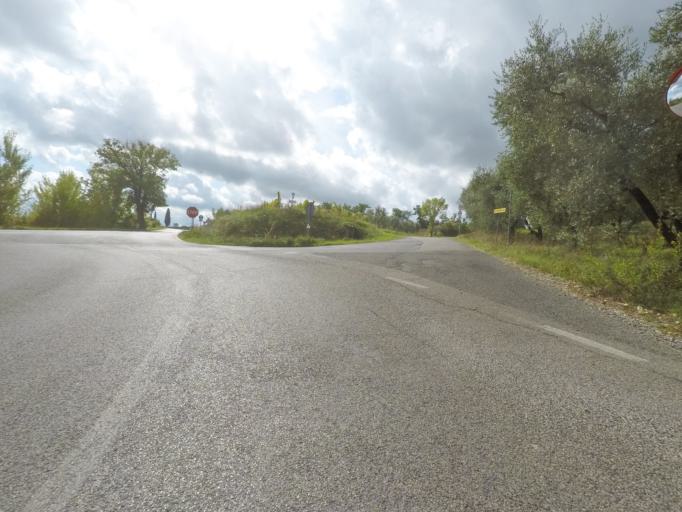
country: IT
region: Tuscany
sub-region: Provincia di Siena
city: Torrita di Siena
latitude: 43.1537
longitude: 11.7770
